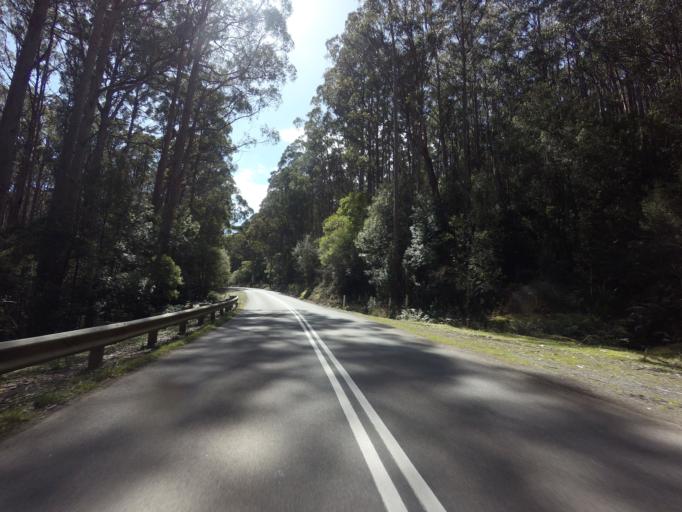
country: AU
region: Tasmania
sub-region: Derwent Valley
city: New Norfolk
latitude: -42.7383
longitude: 146.6636
